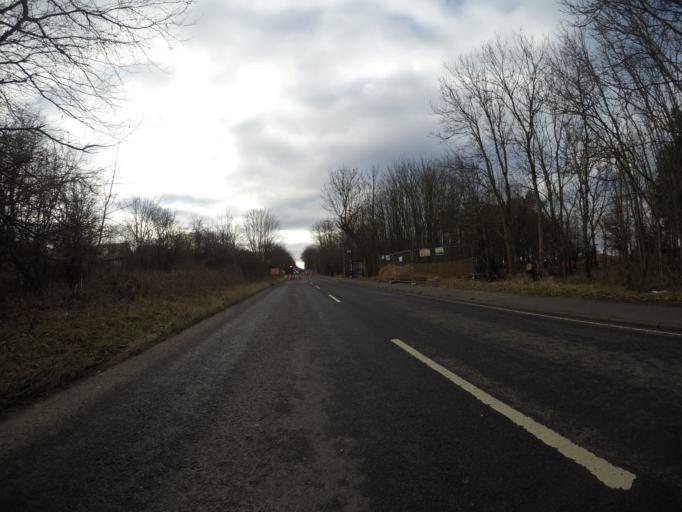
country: GB
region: Scotland
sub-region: North Ayrshire
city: Dreghorn
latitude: 55.5858
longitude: -4.6474
